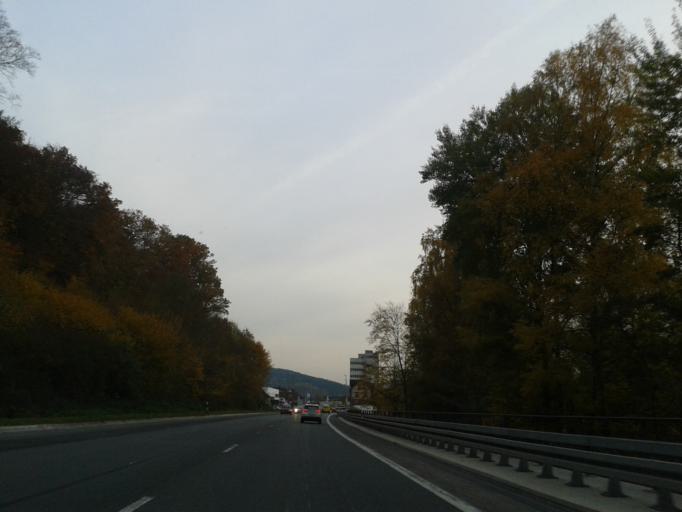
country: DE
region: Hesse
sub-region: Regierungsbezirk Giessen
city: Sinn
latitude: 50.6607
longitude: 8.3257
